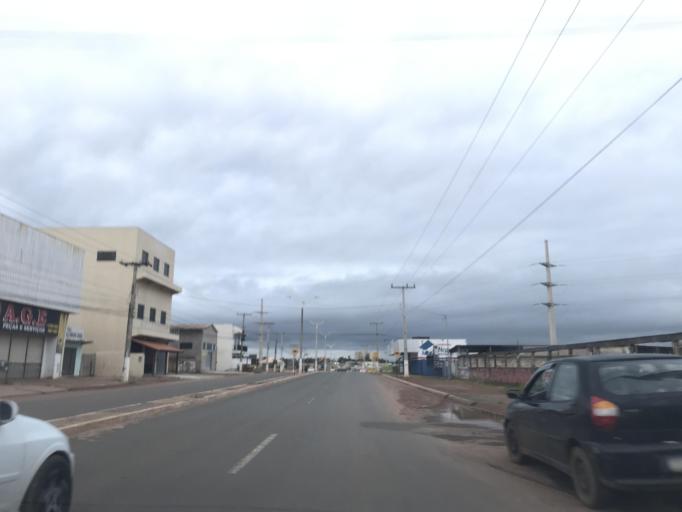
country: BR
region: Goias
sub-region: Luziania
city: Luziania
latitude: -16.2359
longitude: -47.9416
